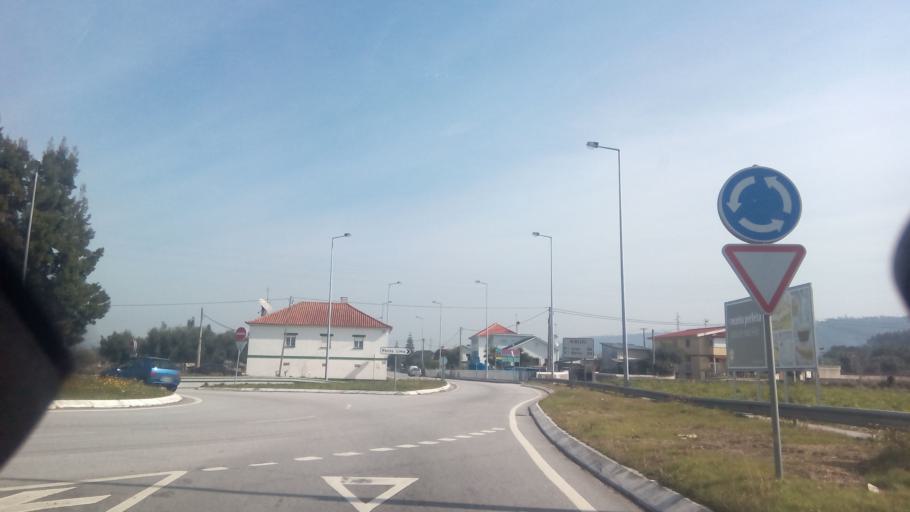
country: PT
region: Viana do Castelo
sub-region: Viana do Castelo
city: Darque
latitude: 41.6810
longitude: -8.7645
